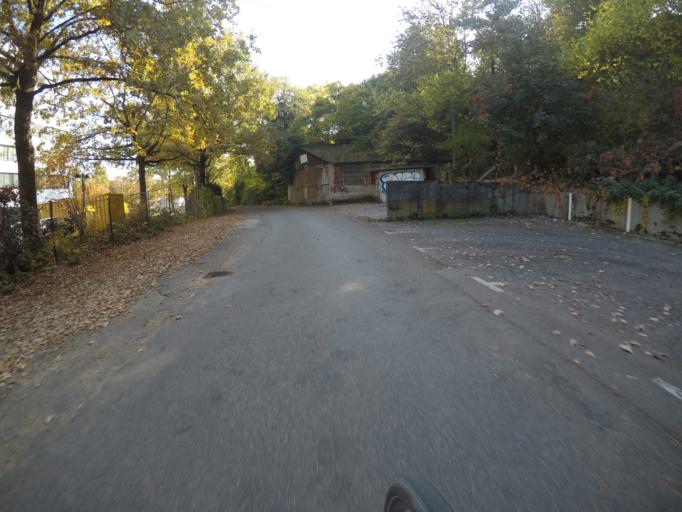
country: DE
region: Baden-Wuerttemberg
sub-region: Regierungsbezirk Stuttgart
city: Stuttgart-Ost
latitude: 48.7792
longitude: 9.2285
